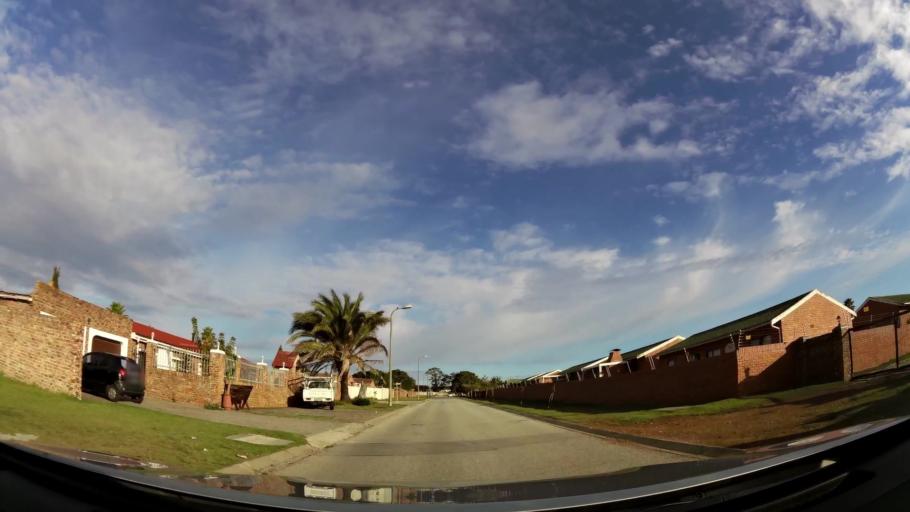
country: ZA
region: Eastern Cape
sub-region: Nelson Mandela Bay Metropolitan Municipality
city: Port Elizabeth
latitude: -33.9576
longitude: 25.4880
